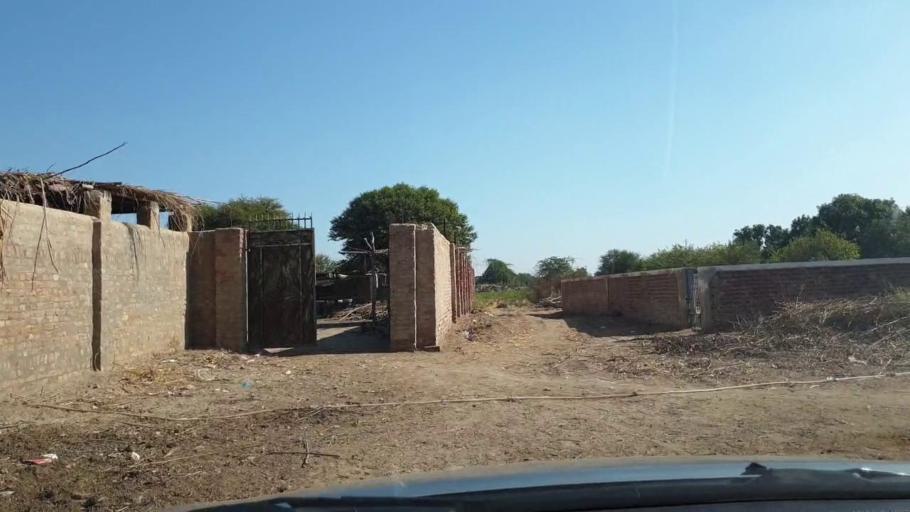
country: PK
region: Sindh
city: Jhol
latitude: 25.9338
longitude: 68.9497
